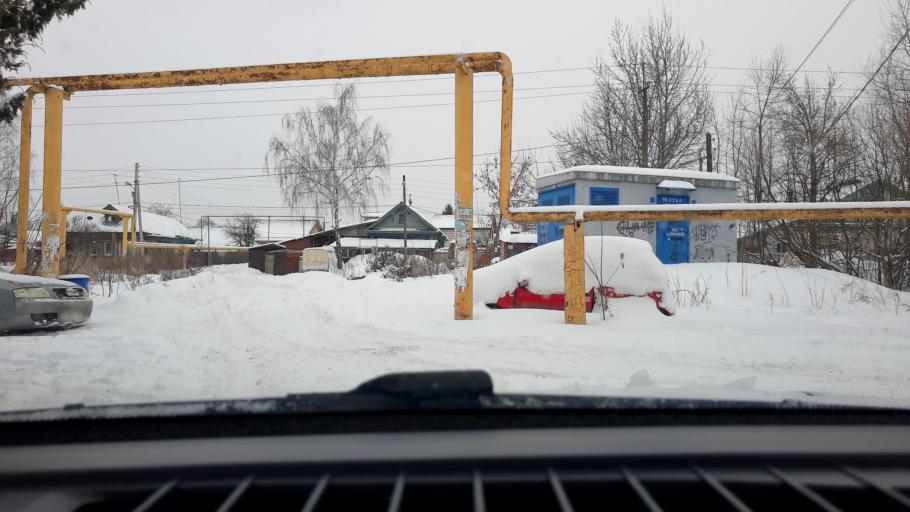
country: RU
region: Nizjnij Novgorod
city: Gorbatovka
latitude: 56.3775
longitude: 43.8249
